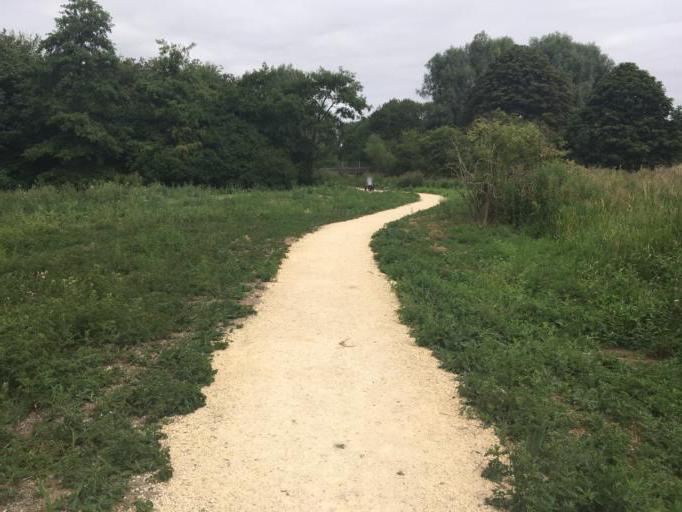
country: GB
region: England
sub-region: Hertfordshire
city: Hemel Hempstead
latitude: 51.7646
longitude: -0.4787
